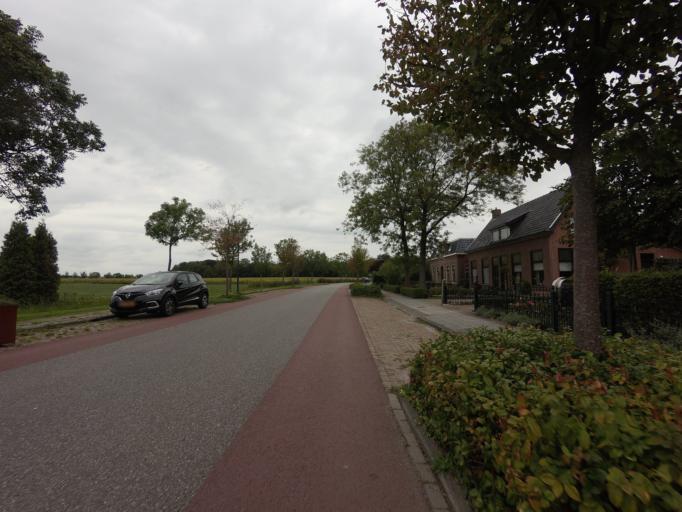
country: NL
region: Friesland
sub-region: Sudwest Fryslan
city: Sneek
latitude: 53.0402
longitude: 5.6377
